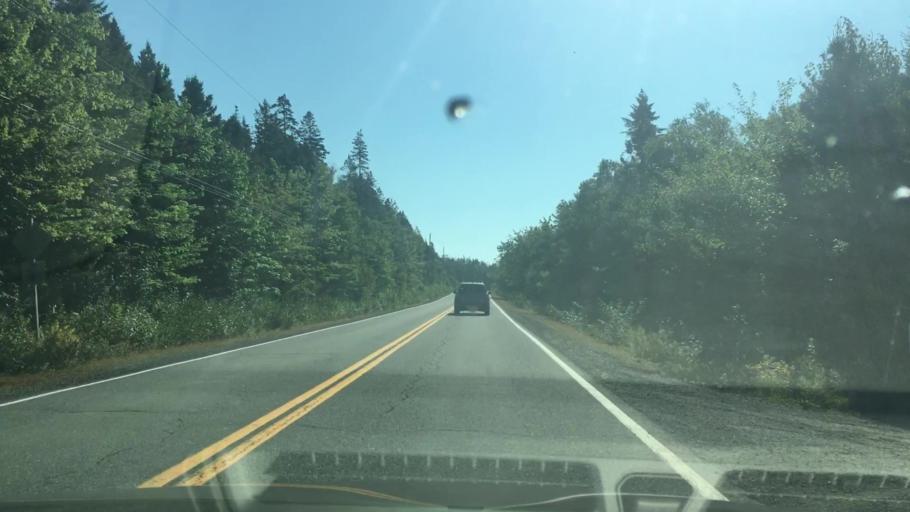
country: CA
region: Nova Scotia
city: Cole Harbour
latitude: 44.8131
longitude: -62.8413
